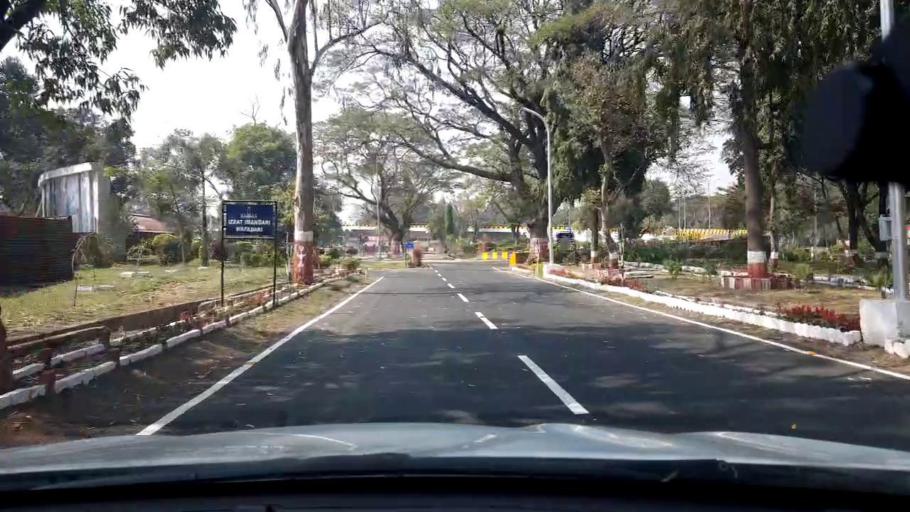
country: IN
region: Maharashtra
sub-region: Pune Division
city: Khadki
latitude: 18.5531
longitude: 73.8669
